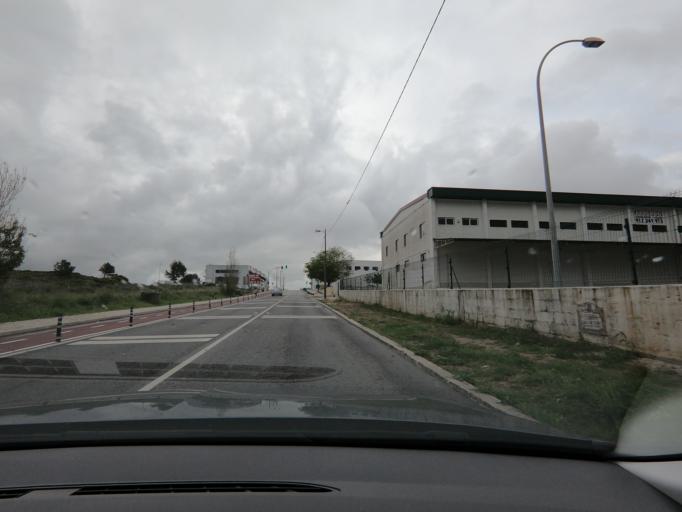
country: PT
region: Lisbon
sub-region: Sintra
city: Sintra
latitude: 38.8016
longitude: -9.3719
